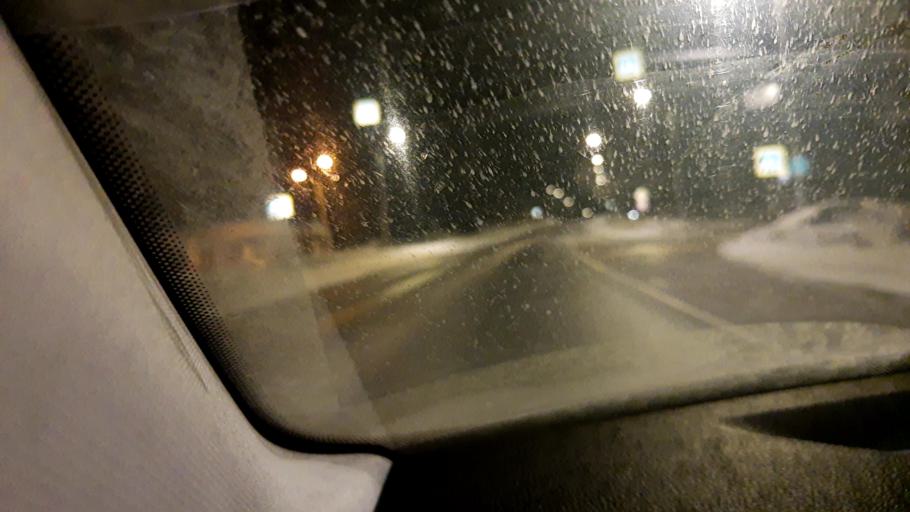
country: RU
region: Moskovskaya
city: Peresvet
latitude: 56.4496
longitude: 38.0991
